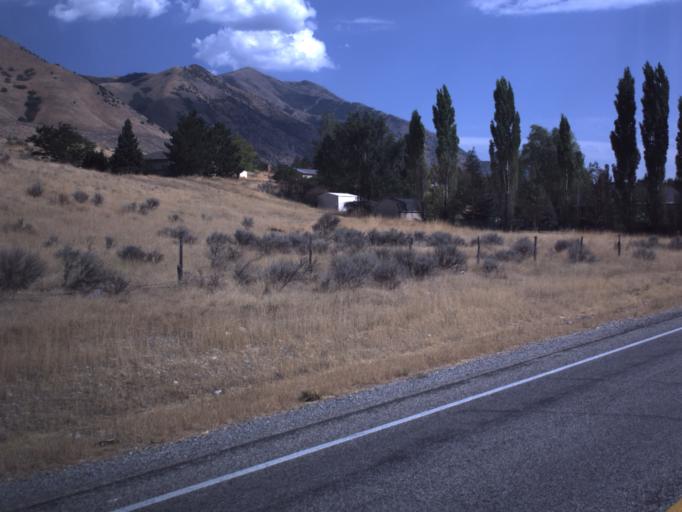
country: US
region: Utah
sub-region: Box Elder County
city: Garland
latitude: 41.7392
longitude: -112.0985
